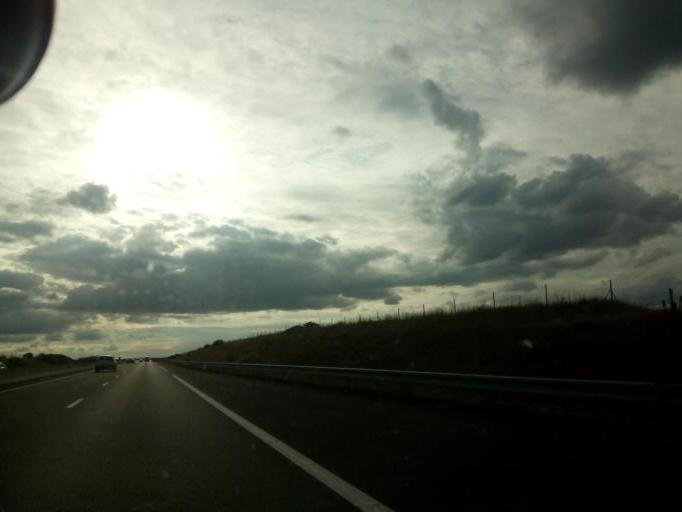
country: FR
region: Centre
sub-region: Departement du Loir-et-Cher
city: Saint-Georges-sur-Cher
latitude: 47.2948
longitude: 1.1413
